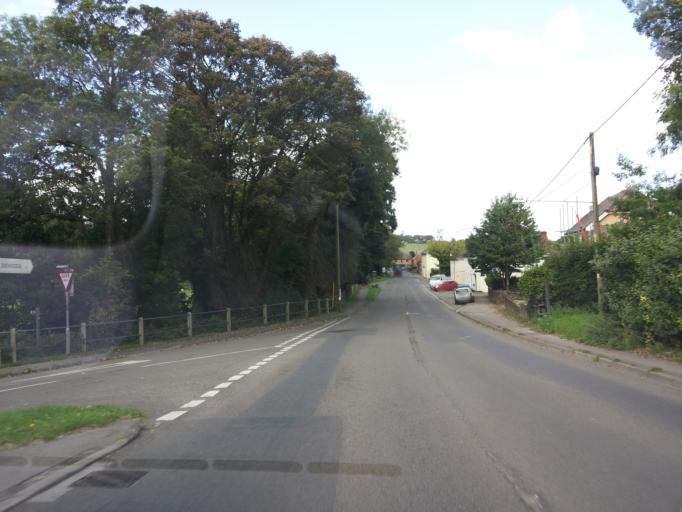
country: GB
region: England
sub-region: Wiltshire
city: Shrewton
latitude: 51.1919
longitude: -1.9024
